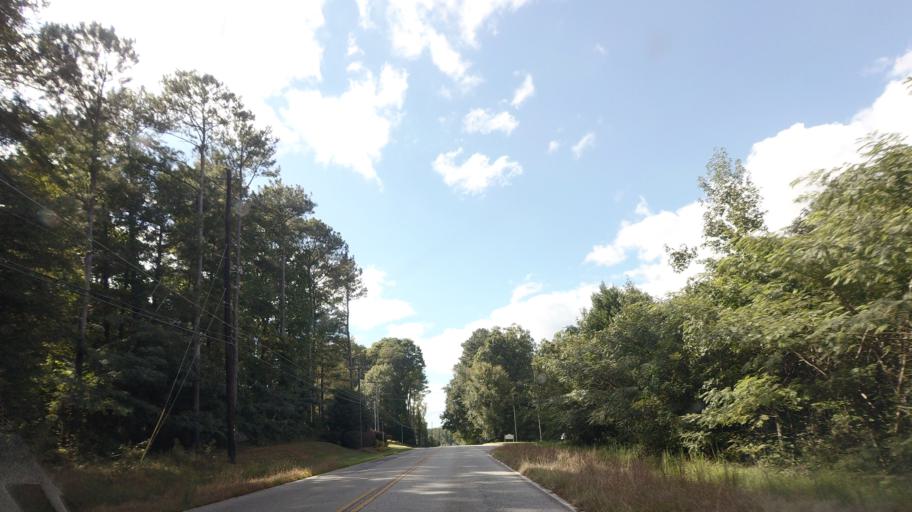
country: US
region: Georgia
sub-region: Bibb County
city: Macon
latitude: 32.9126
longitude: -83.6927
